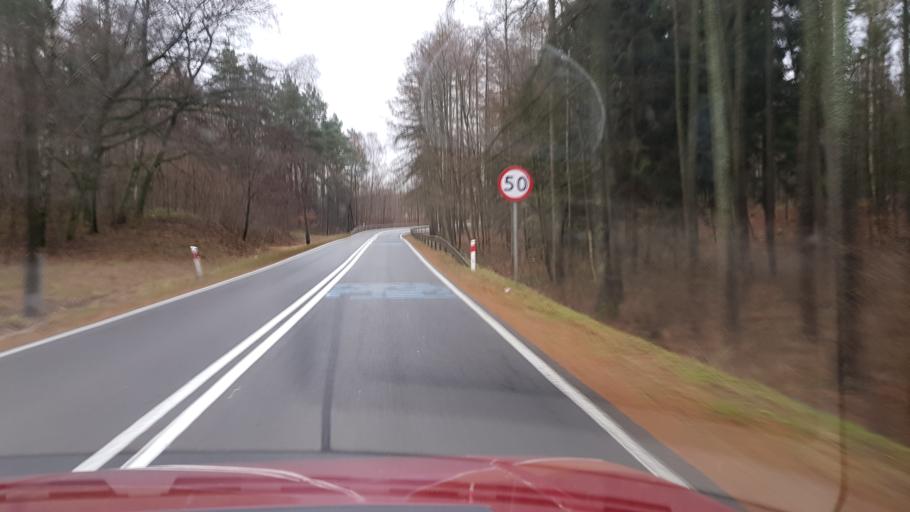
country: PL
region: West Pomeranian Voivodeship
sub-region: Powiat lobeski
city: Wegorzyno
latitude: 53.5247
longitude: 15.6116
